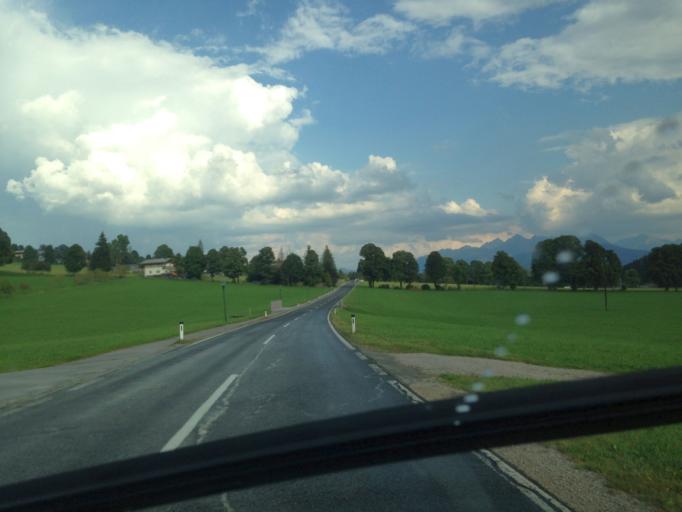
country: AT
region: Styria
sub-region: Politischer Bezirk Liezen
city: Schladming
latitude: 47.4282
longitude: 13.6150
